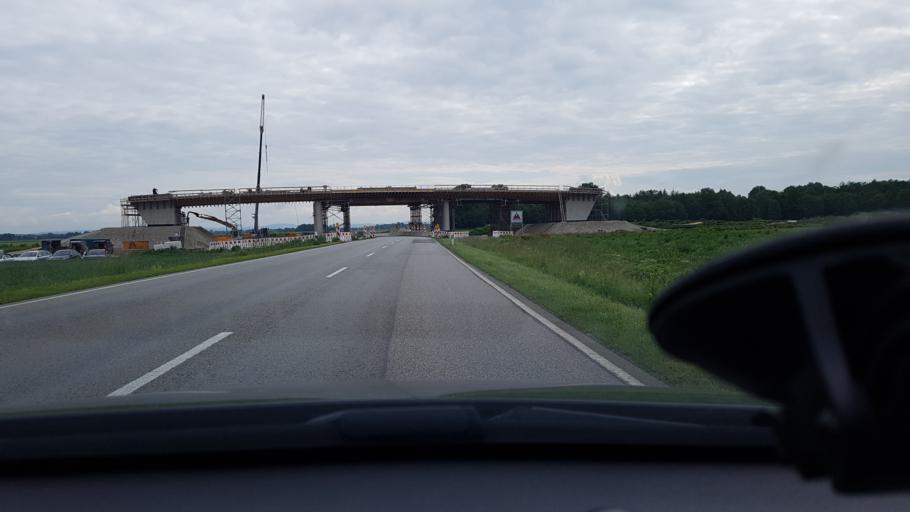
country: DE
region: Bavaria
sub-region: Lower Bavaria
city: Kirchham
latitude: 48.3611
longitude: 13.2622
